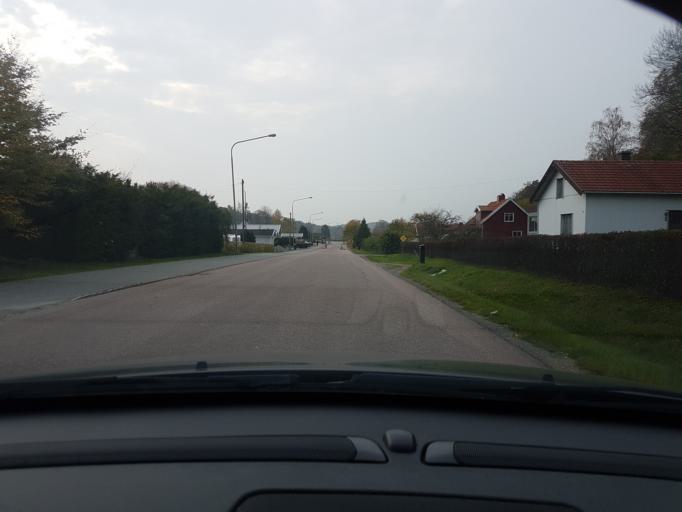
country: SE
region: Vaestra Goetaland
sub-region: Ale Kommun
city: Alvangen
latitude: 57.9508
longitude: 12.1084
